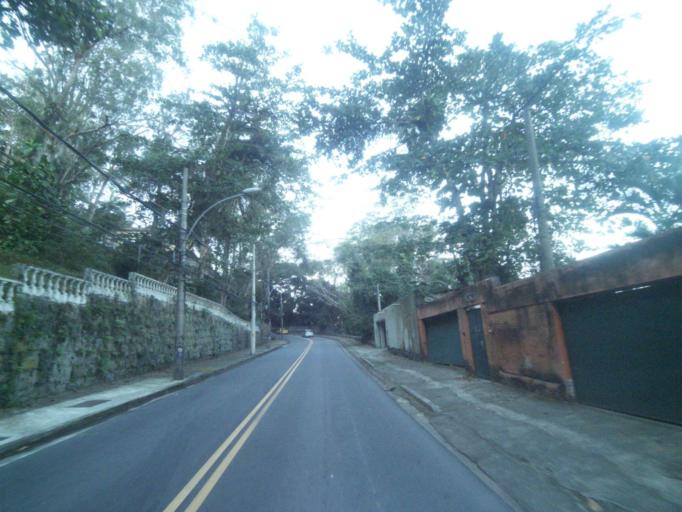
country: BR
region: Rio de Janeiro
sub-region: Rio De Janeiro
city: Rio de Janeiro
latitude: -23.0055
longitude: -43.2825
